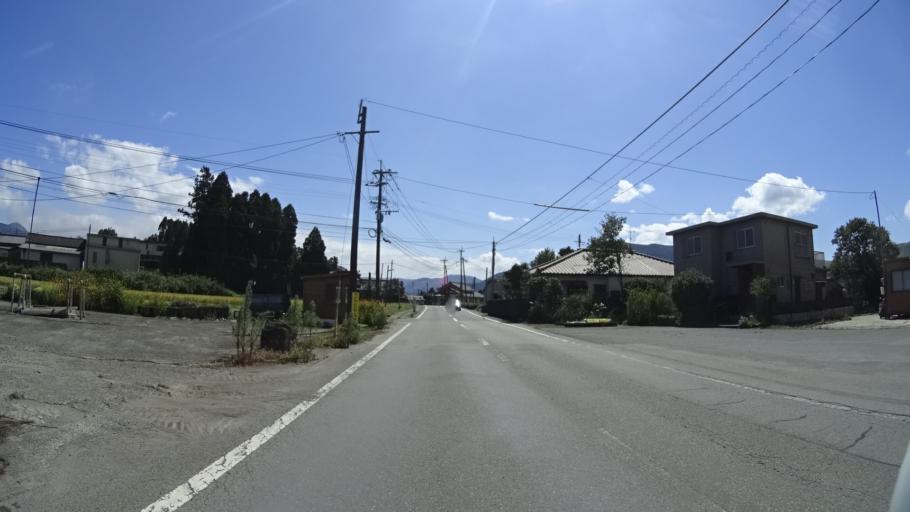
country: JP
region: Kumamoto
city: Aso
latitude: 32.9214
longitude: 130.9939
